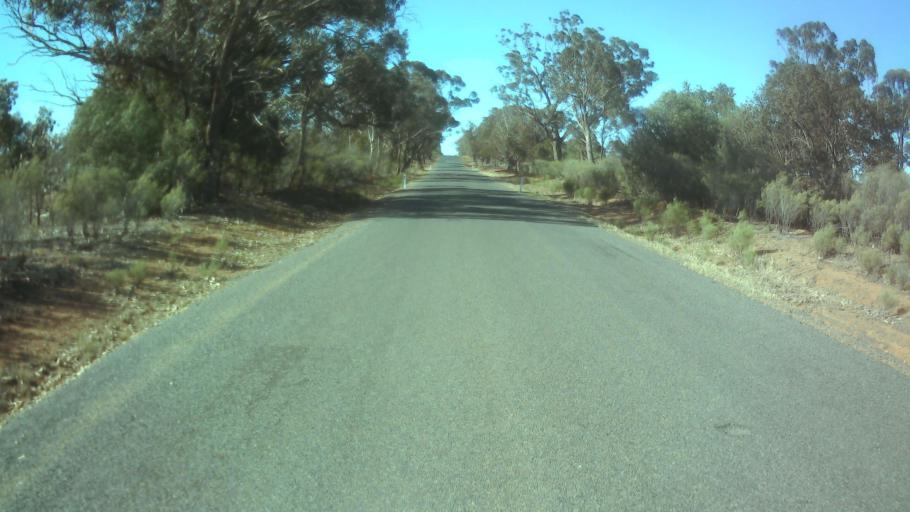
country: AU
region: New South Wales
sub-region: Forbes
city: Forbes
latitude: -33.7081
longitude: 147.8052
